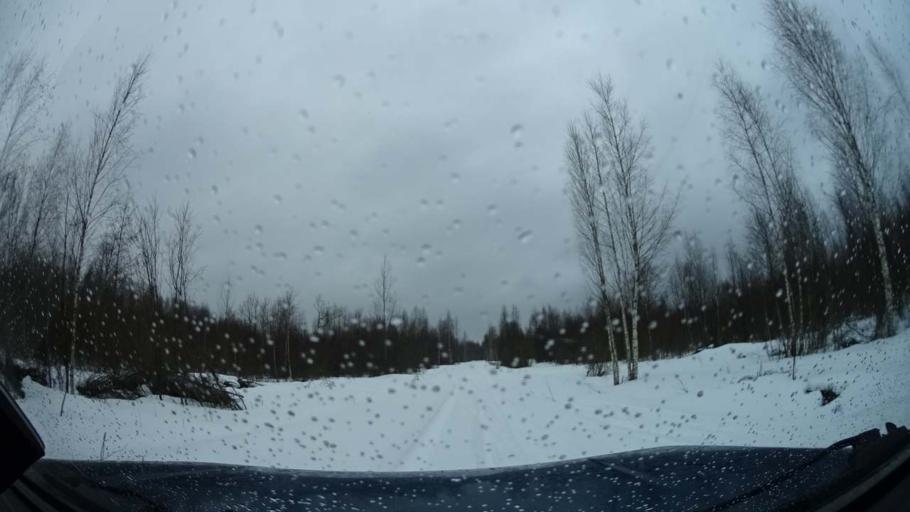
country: RU
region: Tverskaya
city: Gorodnya
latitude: 56.8389
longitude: 36.3974
